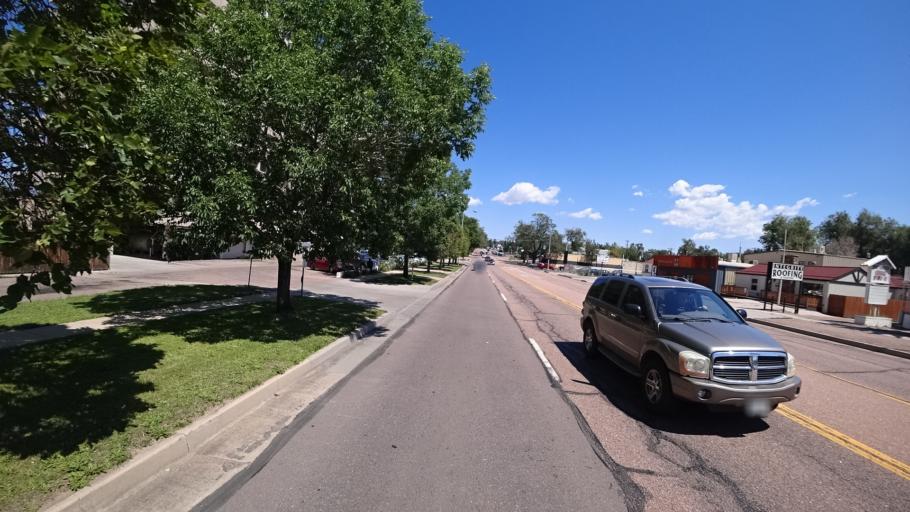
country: US
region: Colorado
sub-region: El Paso County
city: Colorado Springs
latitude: 38.8349
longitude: -104.7947
